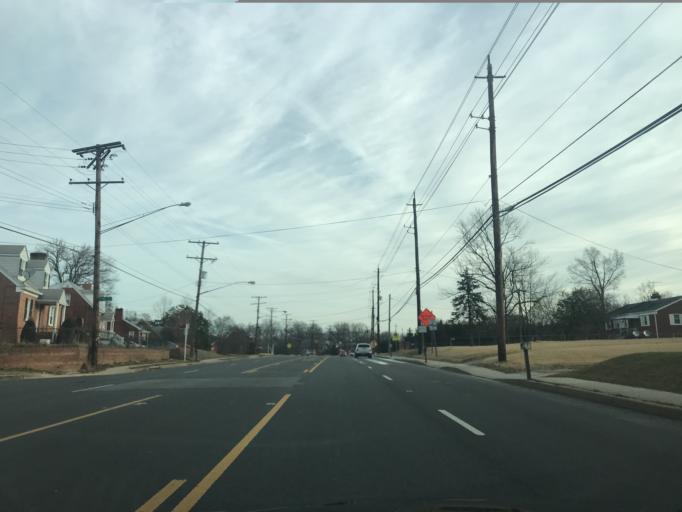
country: US
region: Maryland
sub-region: Prince George's County
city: Hillcrest Heights
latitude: 38.8198
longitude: -76.9580
